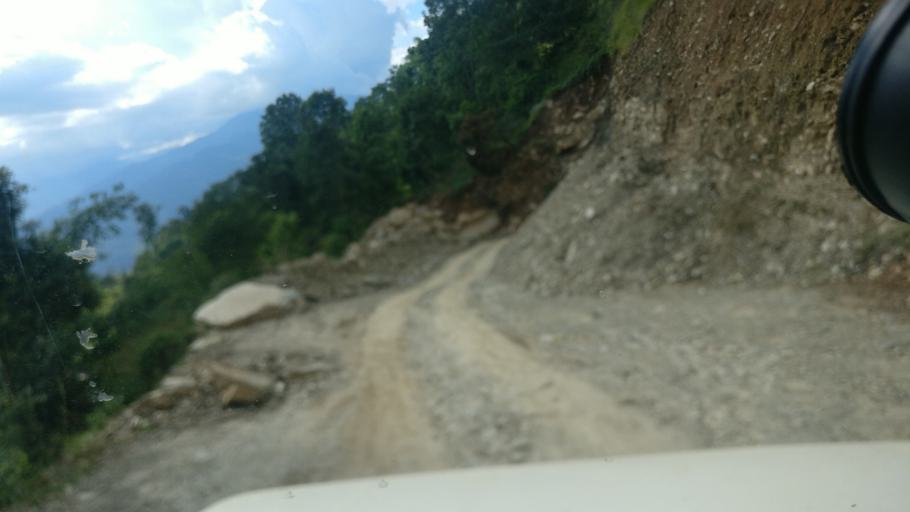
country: NP
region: Western Region
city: Baglung
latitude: 28.2642
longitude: 83.6428
